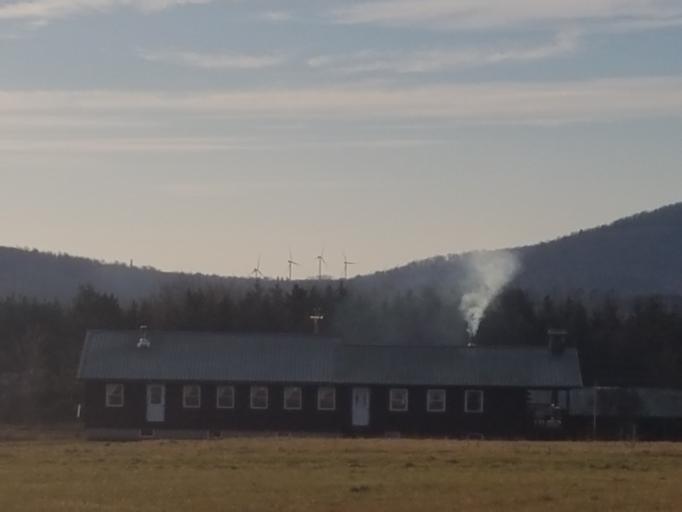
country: US
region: Maine
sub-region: Aroostook County
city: Hodgdon
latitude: 46.1467
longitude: -68.0836
